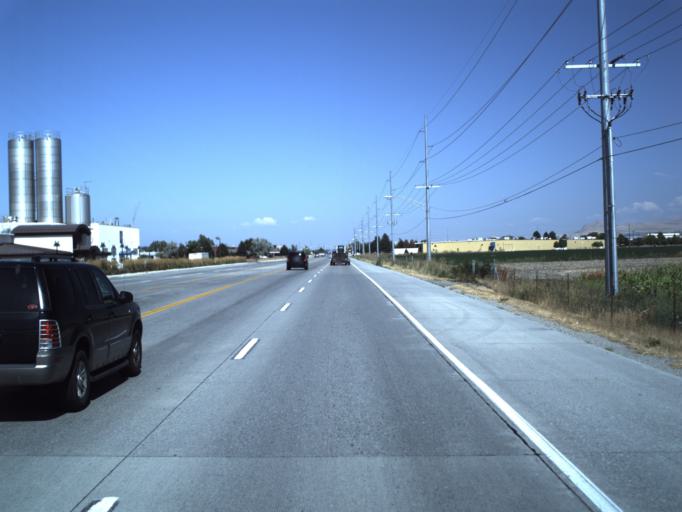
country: US
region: Utah
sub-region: Cache County
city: Logan
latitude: 41.7519
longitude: -111.8589
